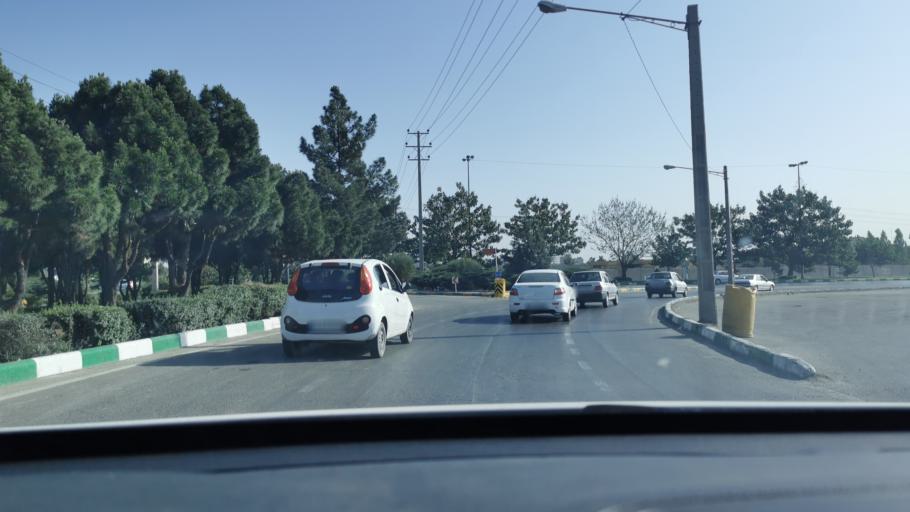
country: IR
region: Razavi Khorasan
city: Mashhad
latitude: 36.3446
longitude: 59.5082
